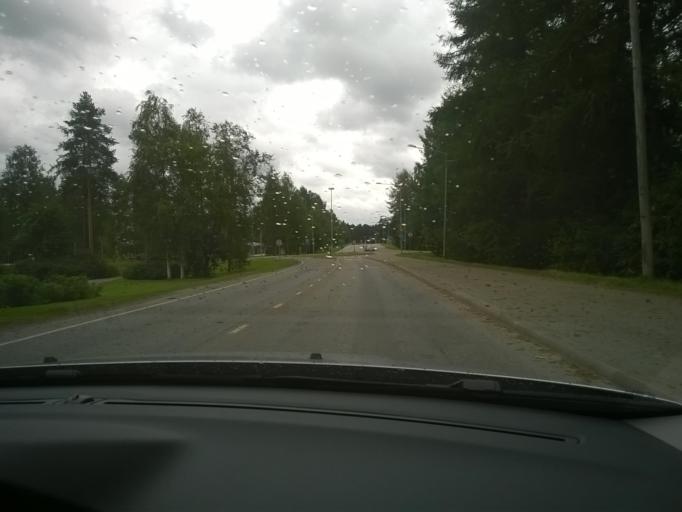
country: FI
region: Kainuu
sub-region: Kehys-Kainuu
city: Kuhmo
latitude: 64.1262
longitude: 29.5028
